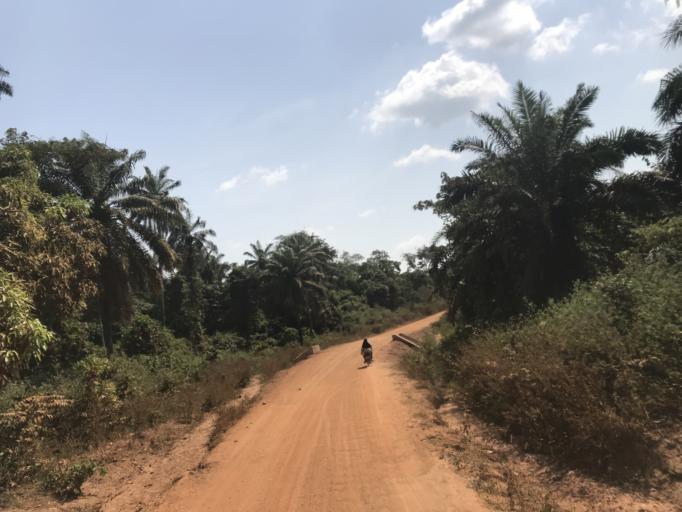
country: NG
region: Osun
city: Ifon
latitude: 7.9190
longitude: 4.4831
